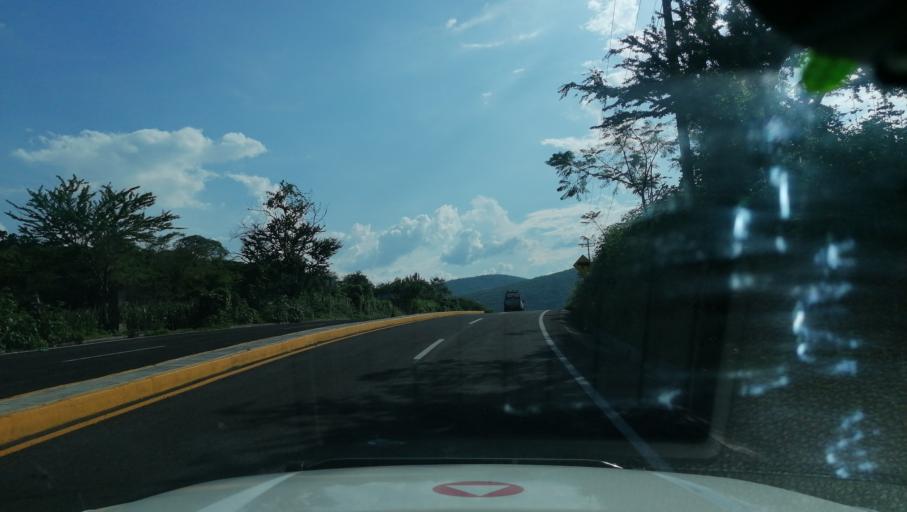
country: MX
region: Morelos
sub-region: Ayala
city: Abelardo L. Rodriguez
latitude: 18.7019
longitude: -98.9918
